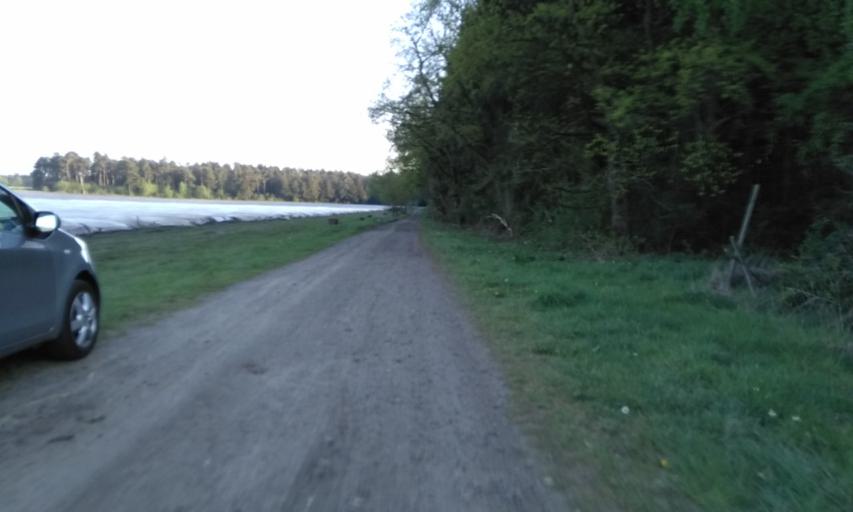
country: DE
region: Lower Saxony
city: Dollern
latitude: 53.5287
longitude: 9.5436
